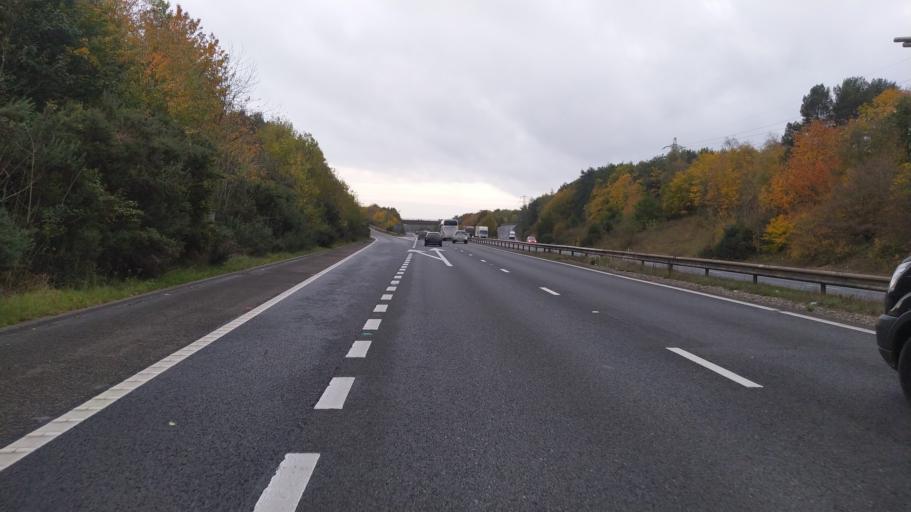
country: GB
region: England
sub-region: Hampshire
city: Cowplain
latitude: 50.9110
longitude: -0.9989
